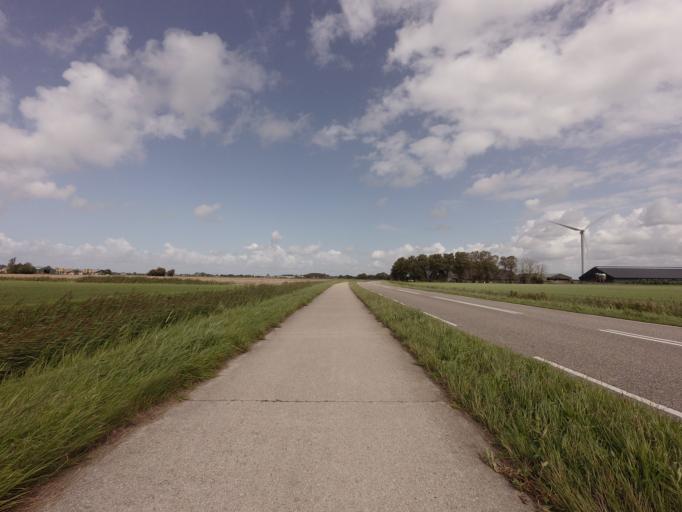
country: NL
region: Friesland
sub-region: Gemeente Harlingen
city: Harlingen
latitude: 53.1382
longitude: 5.4737
